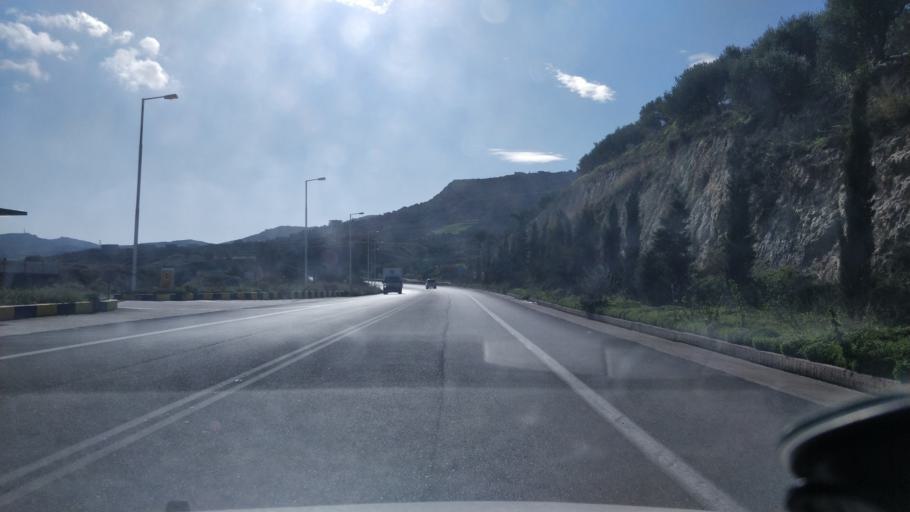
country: GR
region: Crete
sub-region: Nomos Irakleiou
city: Ano Arhanes
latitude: 35.2374
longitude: 25.1804
